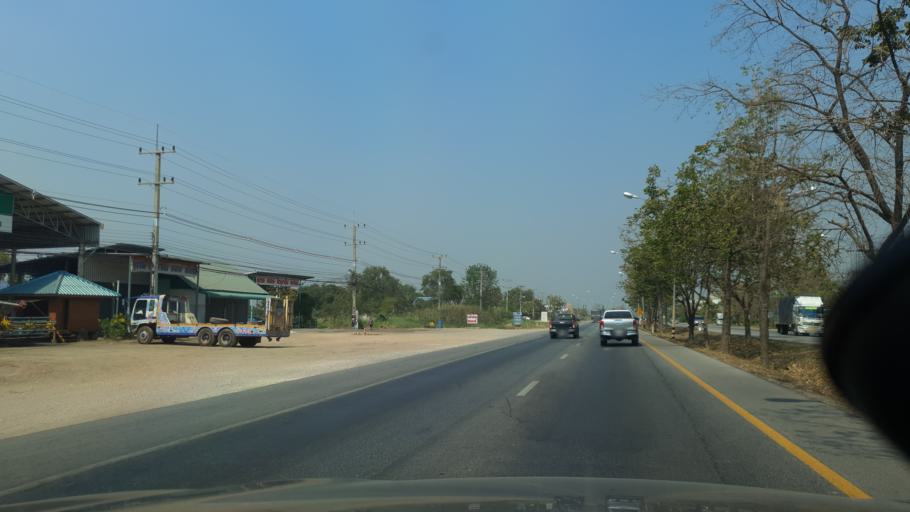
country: TH
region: Kamphaeng Phet
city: Khlong Khlung
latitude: 16.1839
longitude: 99.7128
